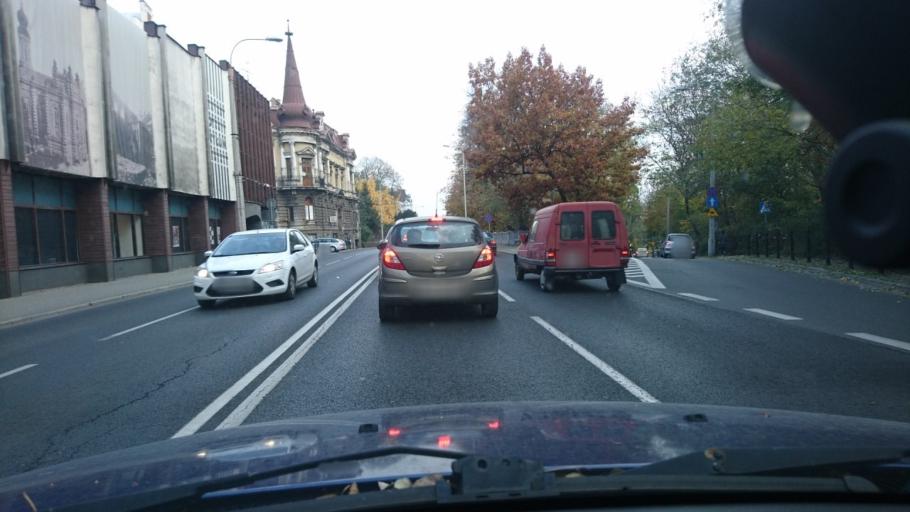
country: PL
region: Silesian Voivodeship
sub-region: Bielsko-Biala
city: Bielsko-Biala
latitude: 49.8244
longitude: 19.0449
